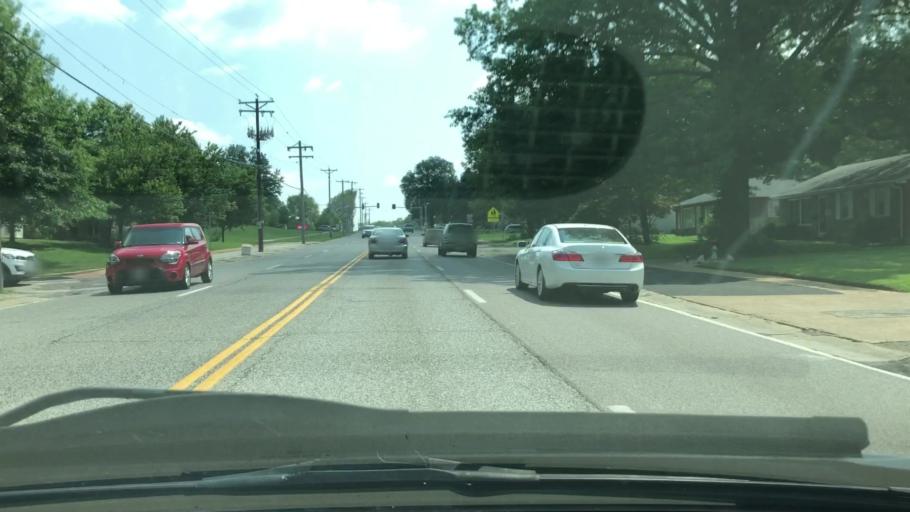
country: US
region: Missouri
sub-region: Saint Louis County
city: Des Peres
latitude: 38.5992
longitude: -90.4216
